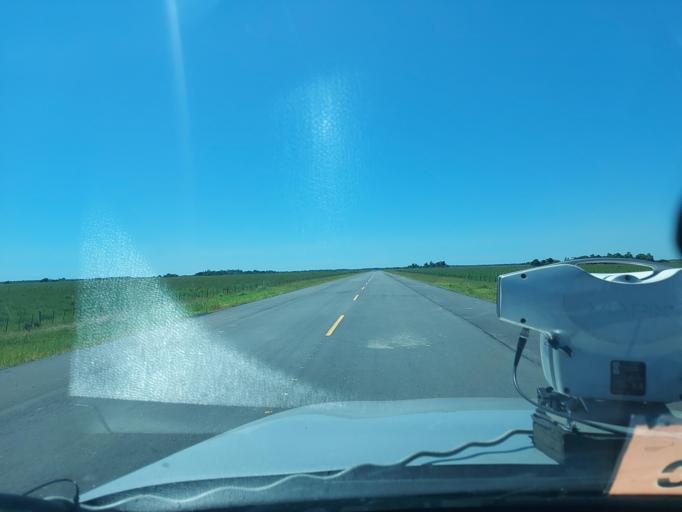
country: PY
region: Neembucu
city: Pilar
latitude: -26.8289
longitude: -58.2379
